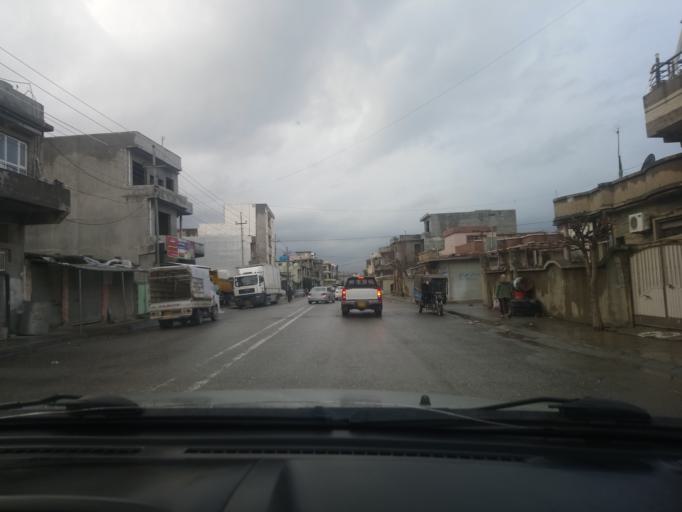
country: IQ
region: As Sulaymaniyah
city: Qeladize
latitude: 36.1835
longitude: 45.1329
